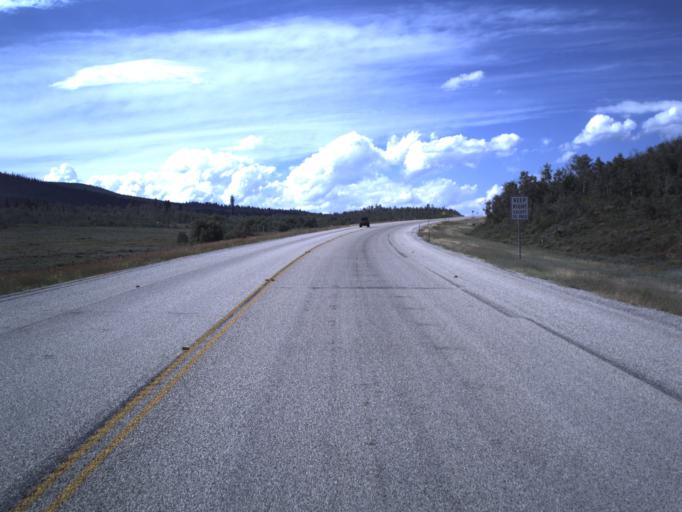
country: US
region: Utah
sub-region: Wasatch County
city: Heber
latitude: 40.2913
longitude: -111.2488
